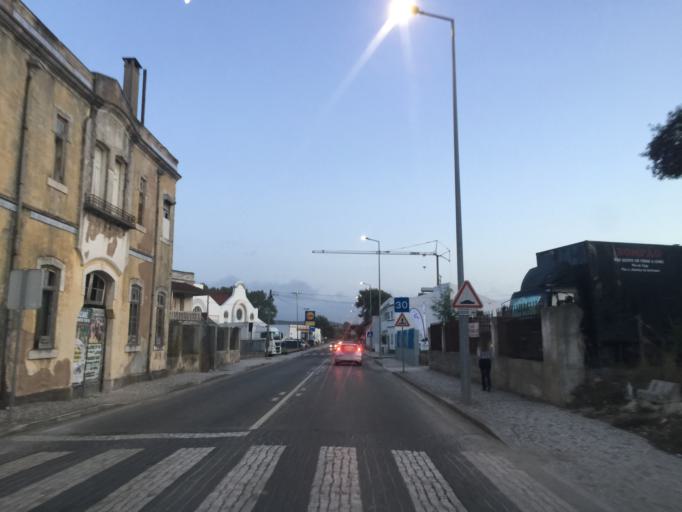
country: PT
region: Leiria
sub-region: Bombarral
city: Bombarral
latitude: 39.2657
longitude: -9.1548
